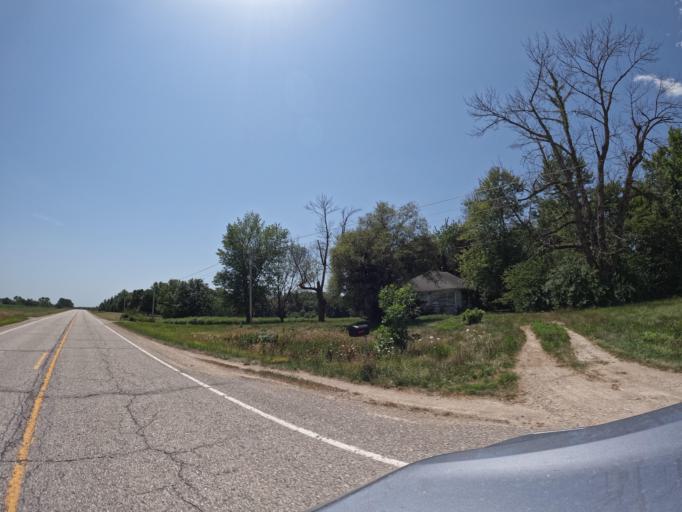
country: US
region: Iowa
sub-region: Henry County
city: Mount Pleasant
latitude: 40.9565
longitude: -91.6124
